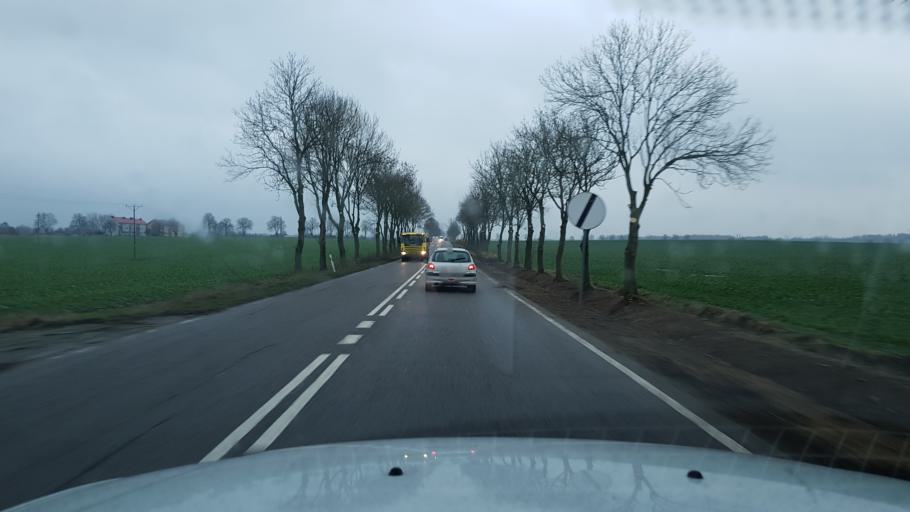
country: PL
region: West Pomeranian Voivodeship
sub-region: Powiat gryficki
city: Ploty
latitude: 53.8490
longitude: 15.2303
